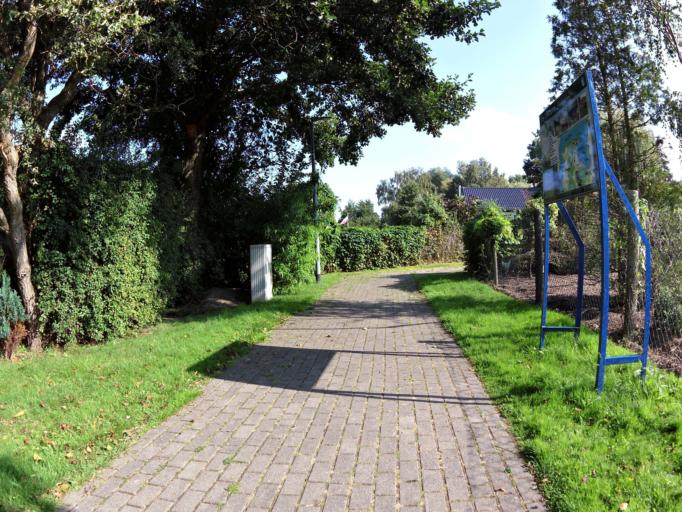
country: DE
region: Mecklenburg-Vorpommern
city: Loddin
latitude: 53.9413
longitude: 14.0415
